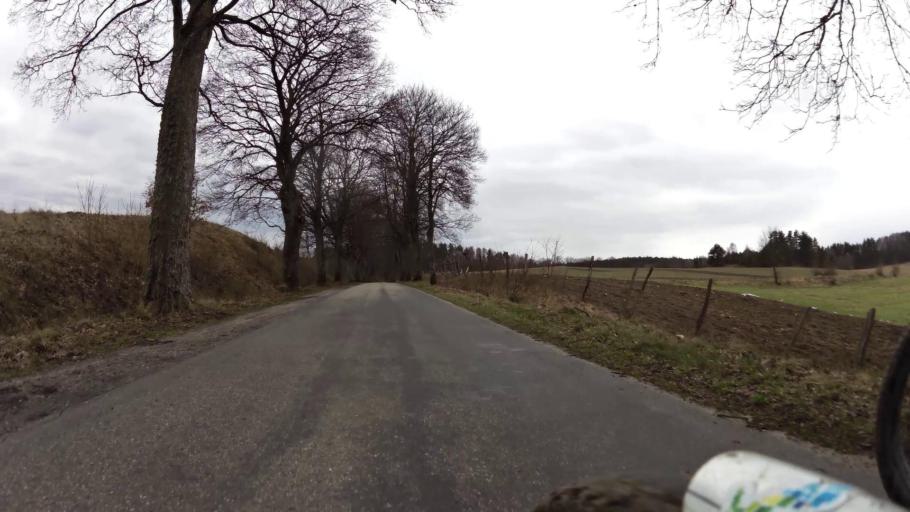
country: PL
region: Pomeranian Voivodeship
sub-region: Powiat bytowski
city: Trzebielino
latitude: 54.1008
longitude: 17.1316
